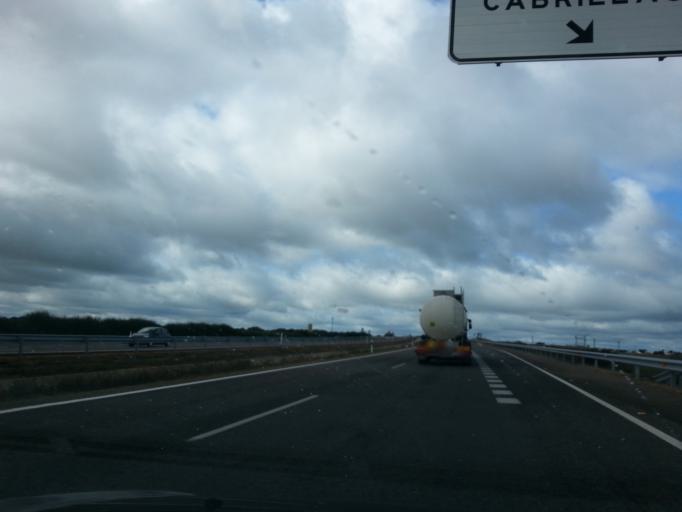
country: ES
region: Castille and Leon
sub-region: Provincia de Salamanca
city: La Fuente de San Esteban
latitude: 40.7894
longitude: -6.2335
